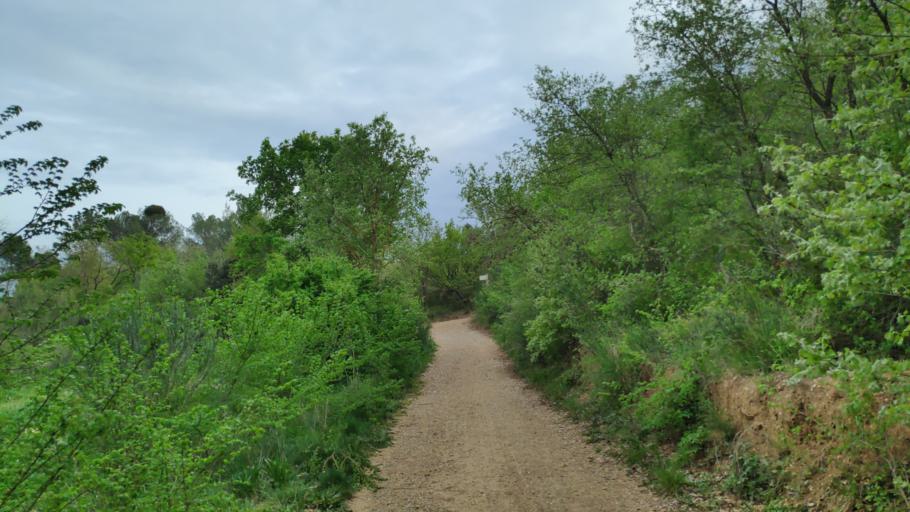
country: ES
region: Catalonia
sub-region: Provincia de Barcelona
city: Sant Quirze del Valles
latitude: 41.5310
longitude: 2.0638
